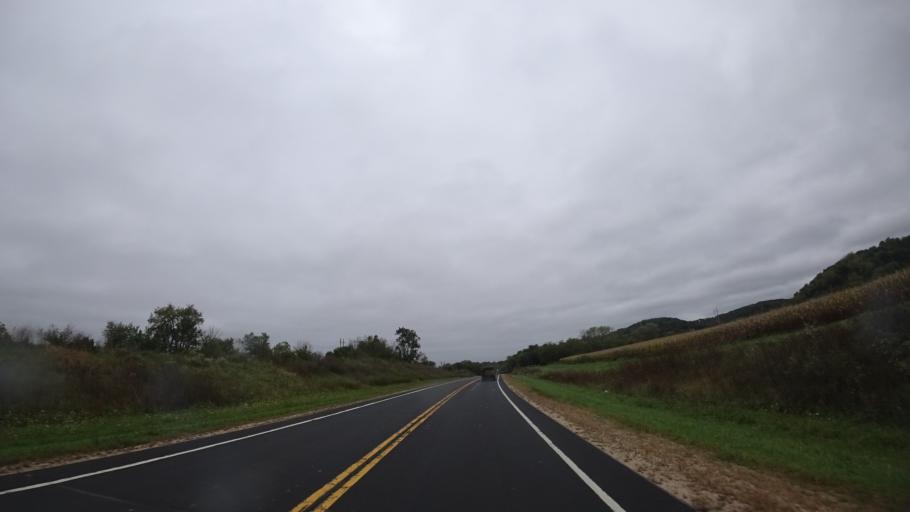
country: US
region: Wisconsin
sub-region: Grant County
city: Boscobel
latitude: 43.1125
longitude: -90.7966
